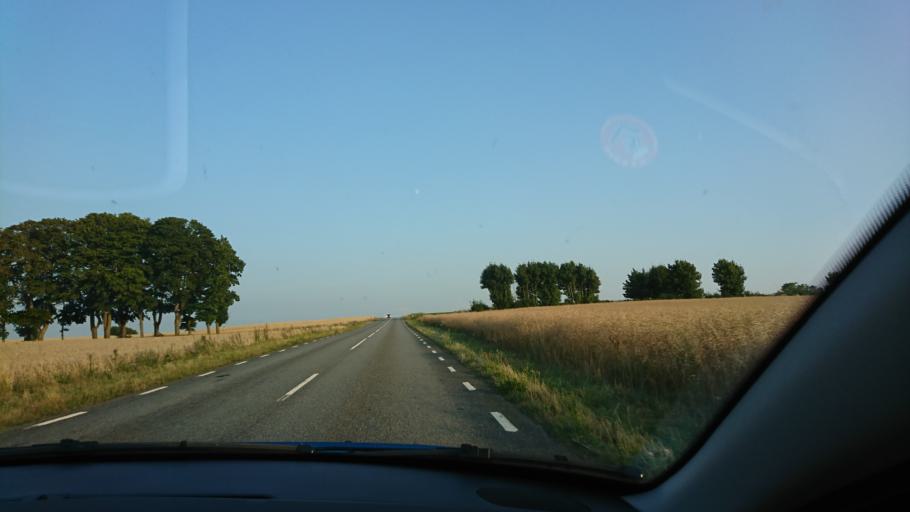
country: SE
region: Skane
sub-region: Simrishamns Kommun
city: Kivik
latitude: 55.6990
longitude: 14.1527
